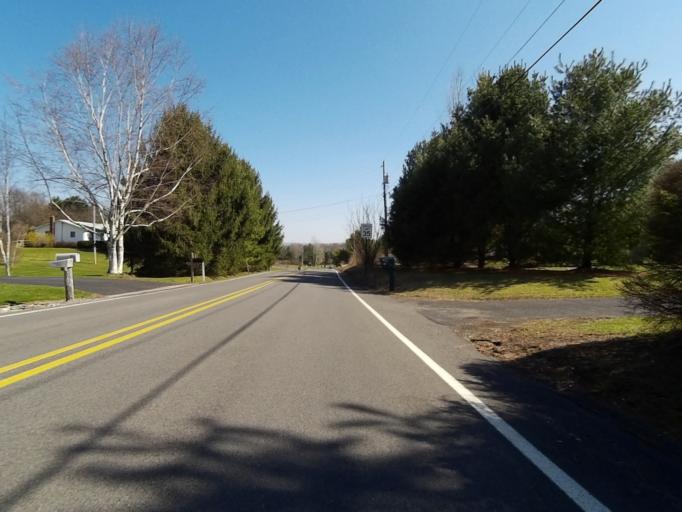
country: US
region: Pennsylvania
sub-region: Centre County
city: Stormstown
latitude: 40.8199
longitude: -77.9745
